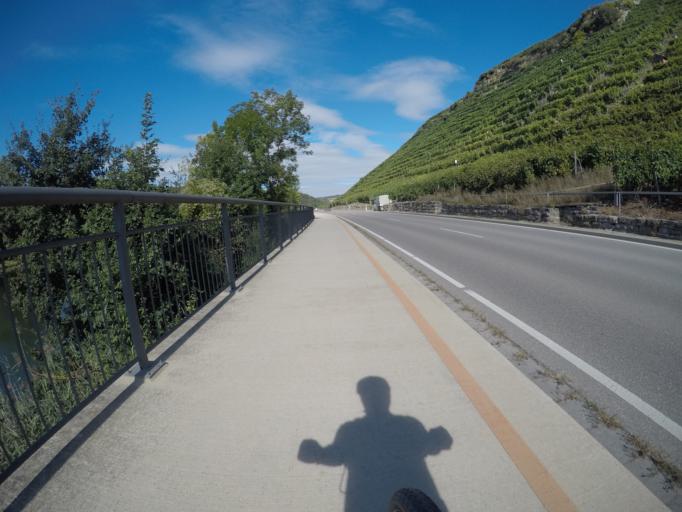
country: DE
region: Baden-Wuerttemberg
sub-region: Regierungsbezirk Stuttgart
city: Mundelsheim
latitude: 48.9844
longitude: 9.2129
